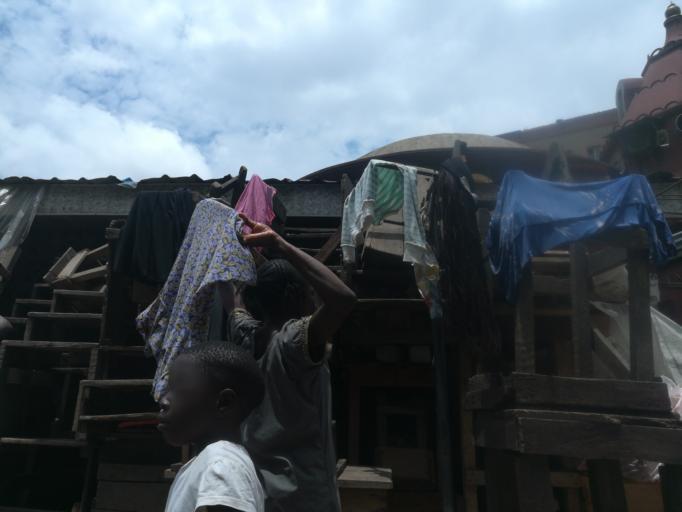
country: NG
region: Lagos
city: Lagos
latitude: 6.4590
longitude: 3.3836
